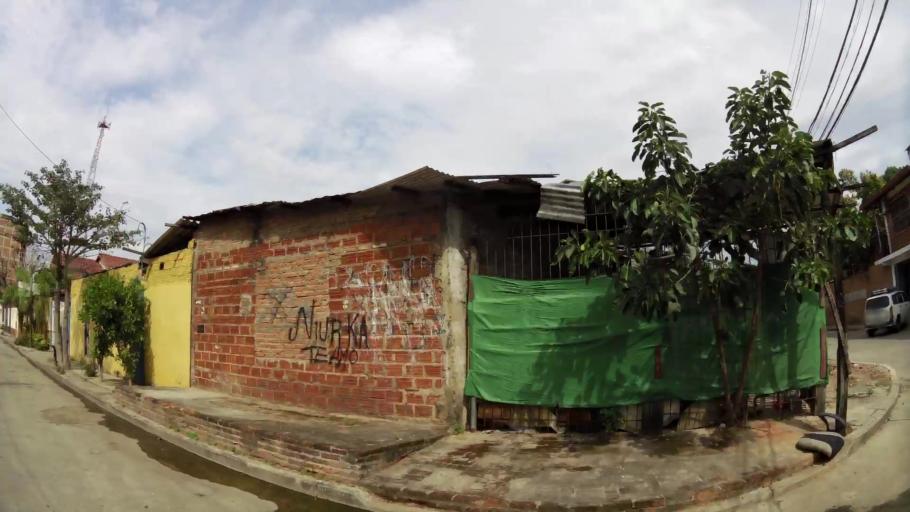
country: BO
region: Santa Cruz
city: Santa Cruz de la Sierra
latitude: -17.7781
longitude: -63.2072
